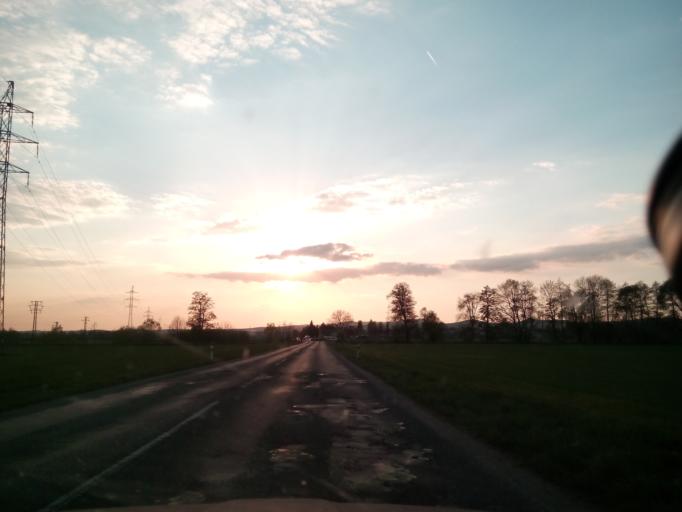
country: SK
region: Trnavsky
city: Vrbove
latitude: 48.5885
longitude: 17.7639
